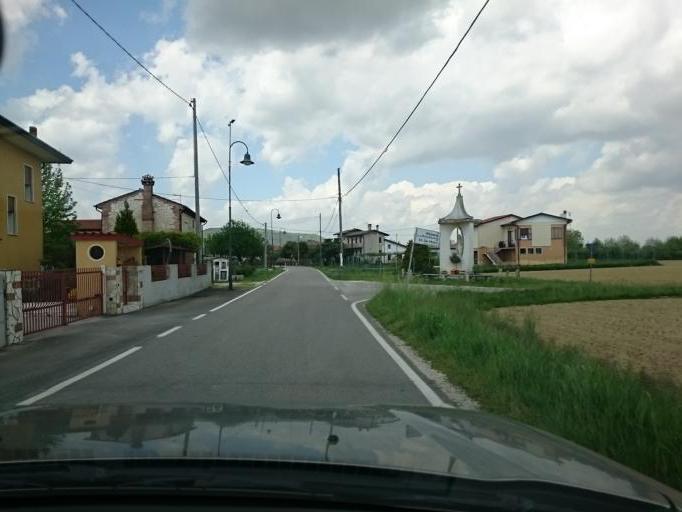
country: IT
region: Veneto
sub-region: Provincia di Vicenza
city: Villaganzerla
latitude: 45.4506
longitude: 11.6365
